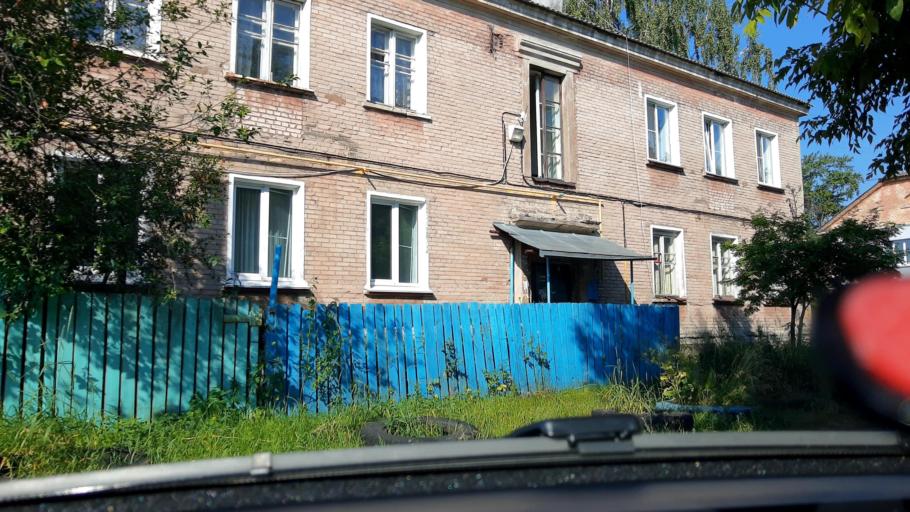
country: RU
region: Nizjnij Novgorod
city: Neklyudovo
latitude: 56.3570
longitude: 43.8471
